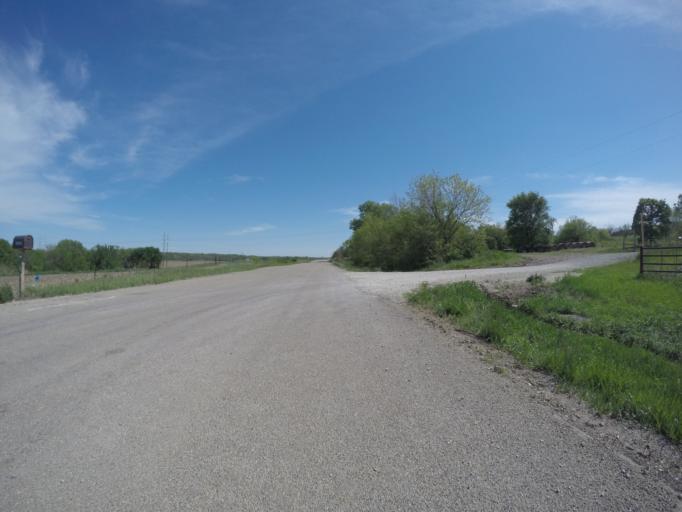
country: US
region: Kansas
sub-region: Riley County
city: Ogden
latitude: 39.0246
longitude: -96.6090
